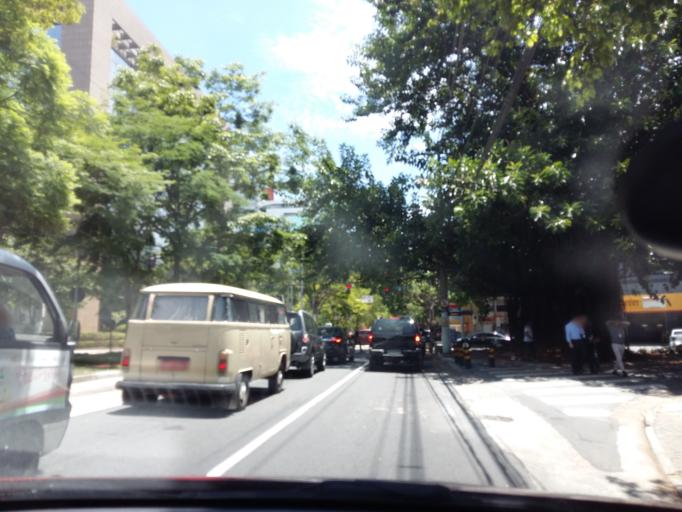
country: BR
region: Sao Paulo
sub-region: Sao Paulo
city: Sao Paulo
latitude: -23.6037
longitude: -46.6922
